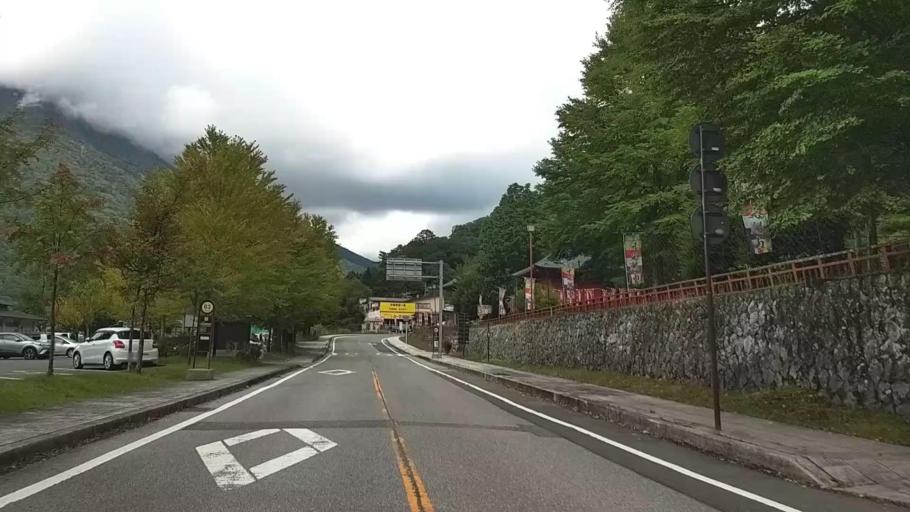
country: JP
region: Tochigi
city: Nikko
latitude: 36.7309
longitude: 139.4910
